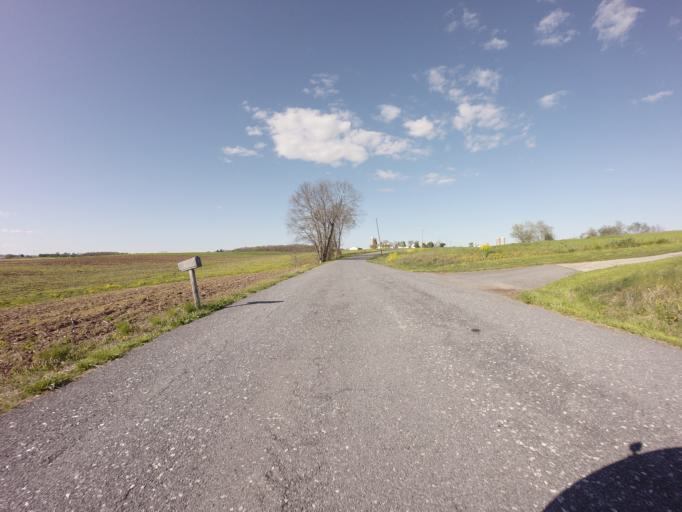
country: US
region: Maryland
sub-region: Frederick County
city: Emmitsburg
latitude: 39.6428
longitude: -77.2970
